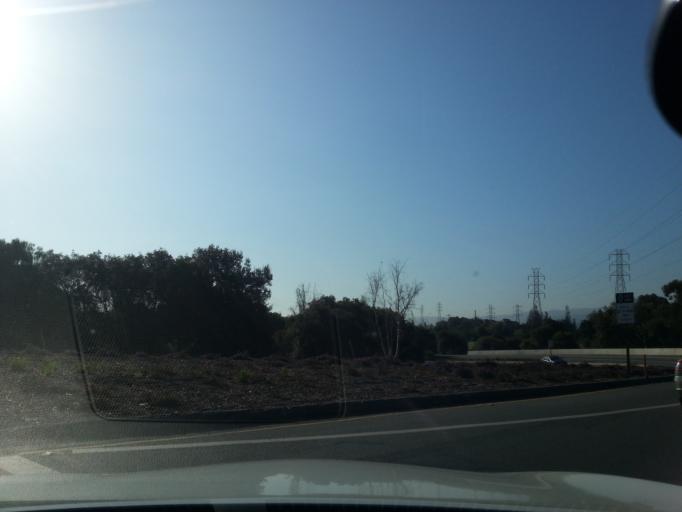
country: US
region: California
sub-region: Santa Clara County
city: Mountain View
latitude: 37.3784
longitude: -122.0688
